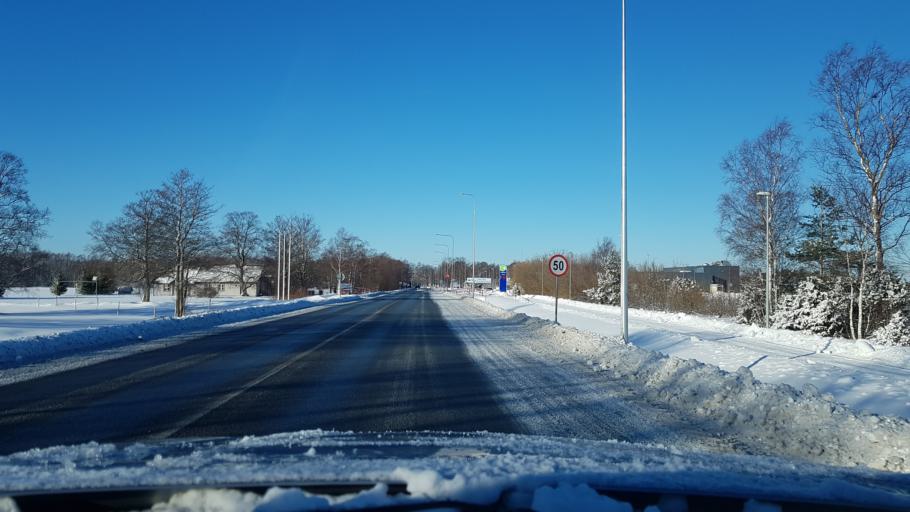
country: EE
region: Hiiumaa
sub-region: Kaerdla linn
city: Kardla
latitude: 58.9884
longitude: 22.7678
